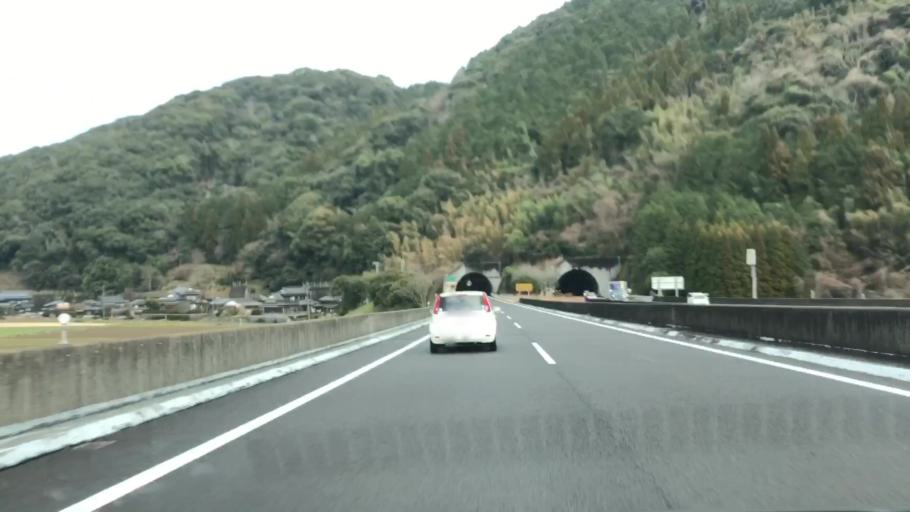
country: JP
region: Saga Prefecture
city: Takeocho-takeo
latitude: 33.1716
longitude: 130.0400
